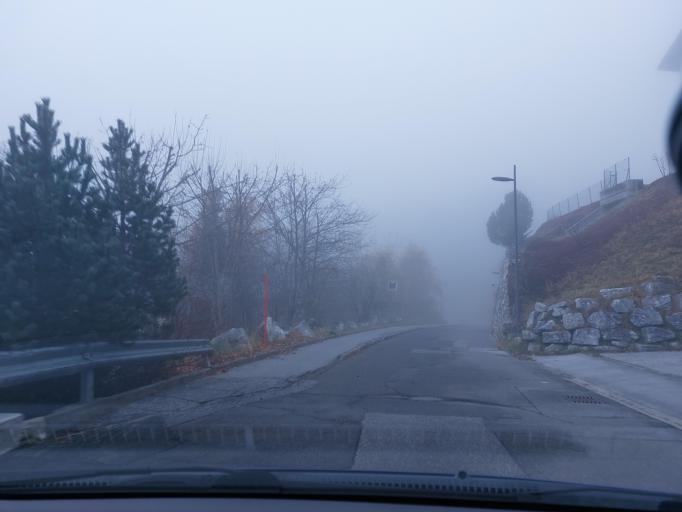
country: CH
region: Valais
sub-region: Sierre District
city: Randogne
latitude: 46.3119
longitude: 7.4888
